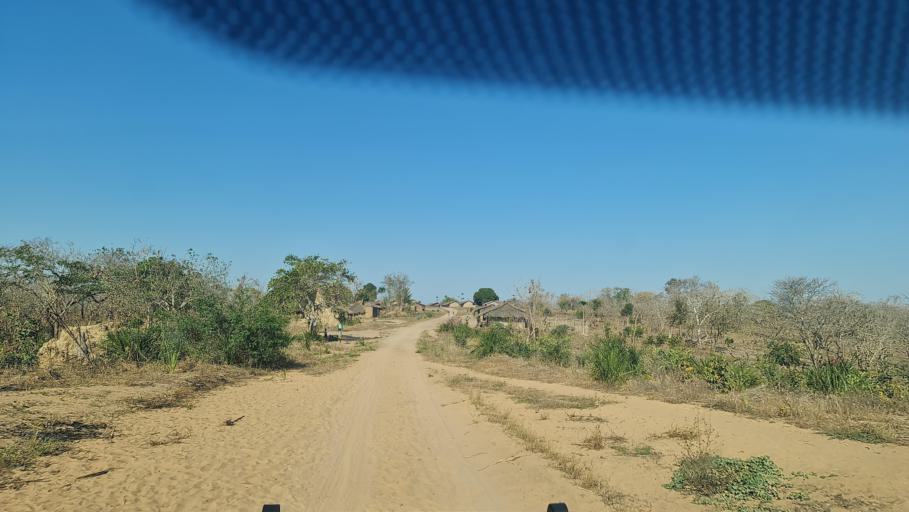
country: MZ
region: Nampula
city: Nacala
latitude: -13.9408
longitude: 40.4870
